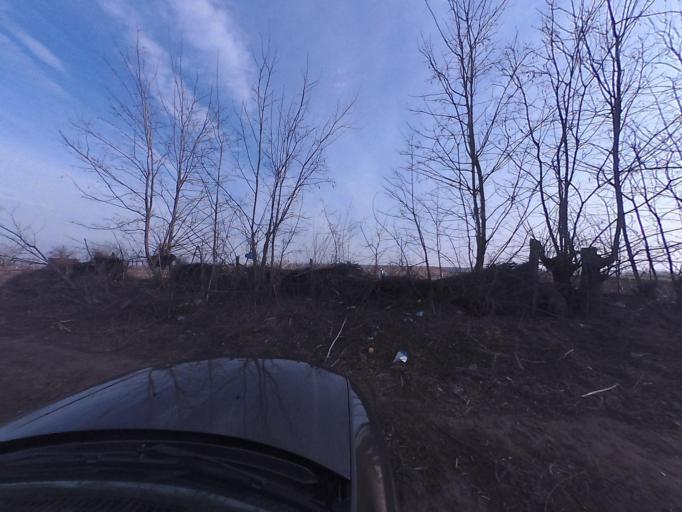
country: RO
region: Vaslui
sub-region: Comuna Solesti
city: Solesti
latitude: 46.8146
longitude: 27.7656
